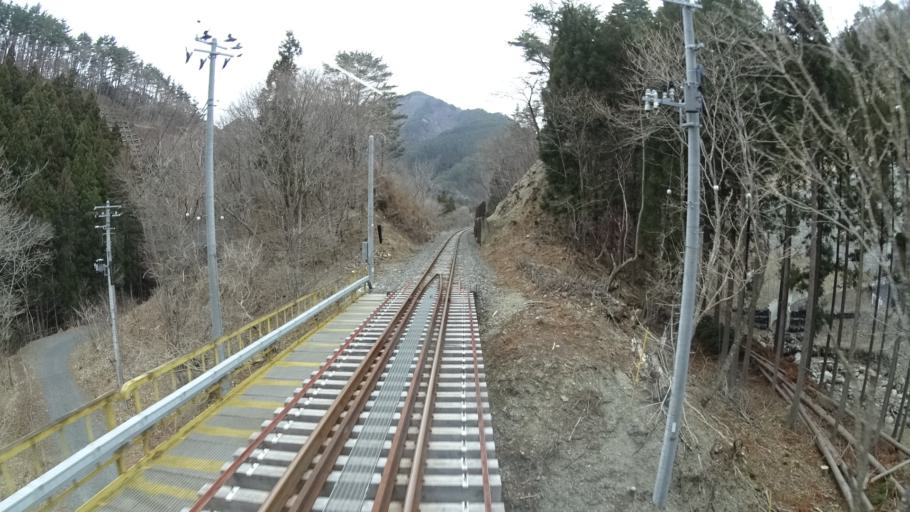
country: JP
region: Iwate
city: Kamaishi
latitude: 39.2895
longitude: 141.8626
